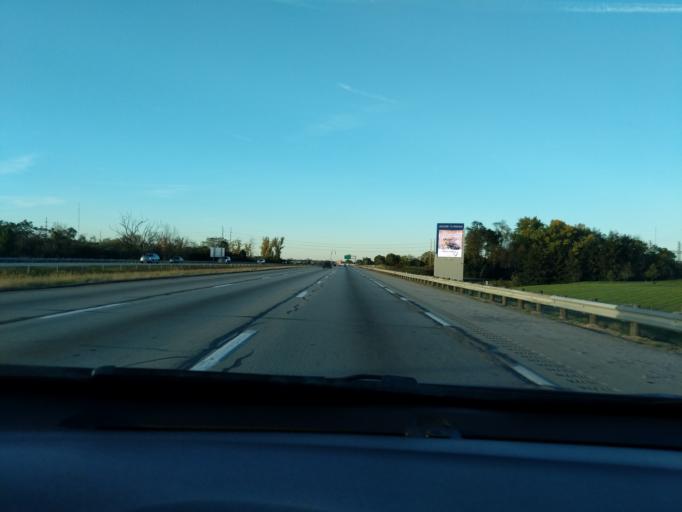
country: US
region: Ohio
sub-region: Montgomery County
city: Moraine
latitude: 39.6983
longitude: -84.2293
